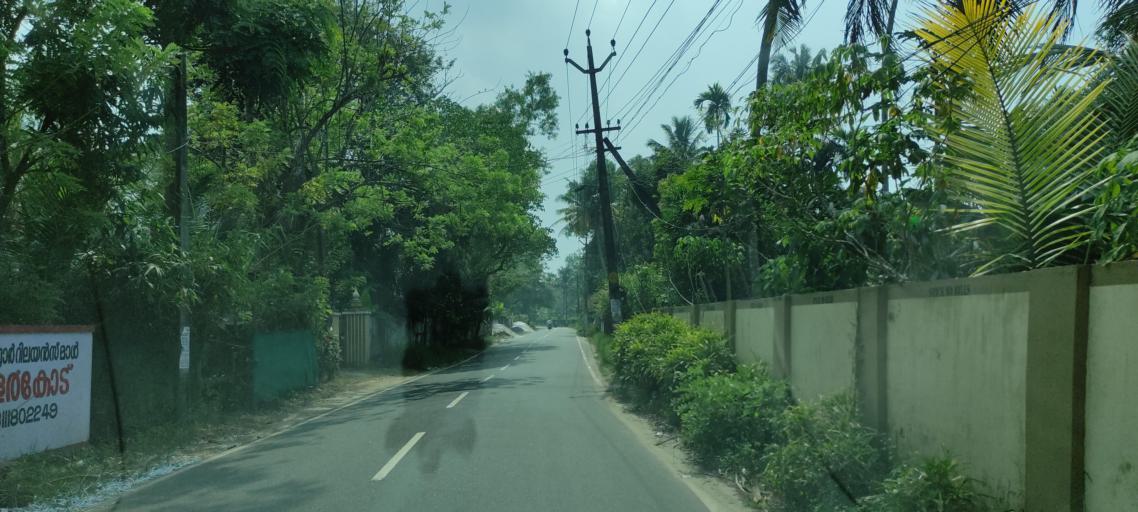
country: IN
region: Kerala
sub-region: Alappuzha
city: Alleppey
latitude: 9.5541
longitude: 76.3334
